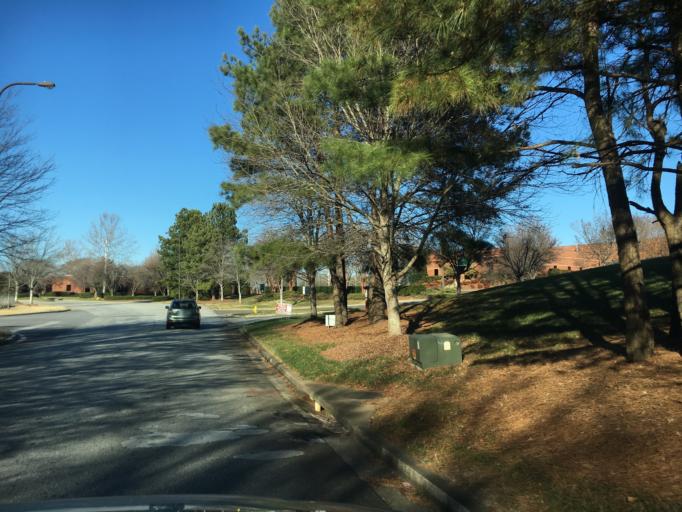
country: US
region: South Carolina
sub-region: Greenville County
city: Mauldin
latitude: 34.8089
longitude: -82.2780
